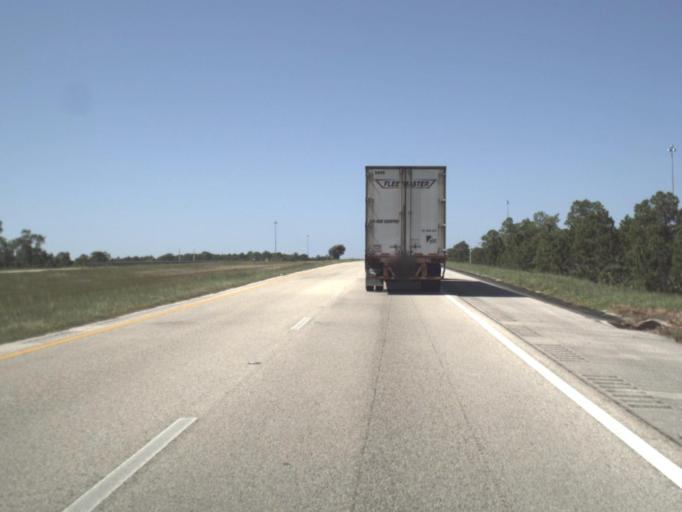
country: US
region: Florida
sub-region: Collier County
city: Golden Gate
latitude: 26.1596
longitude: -81.6831
